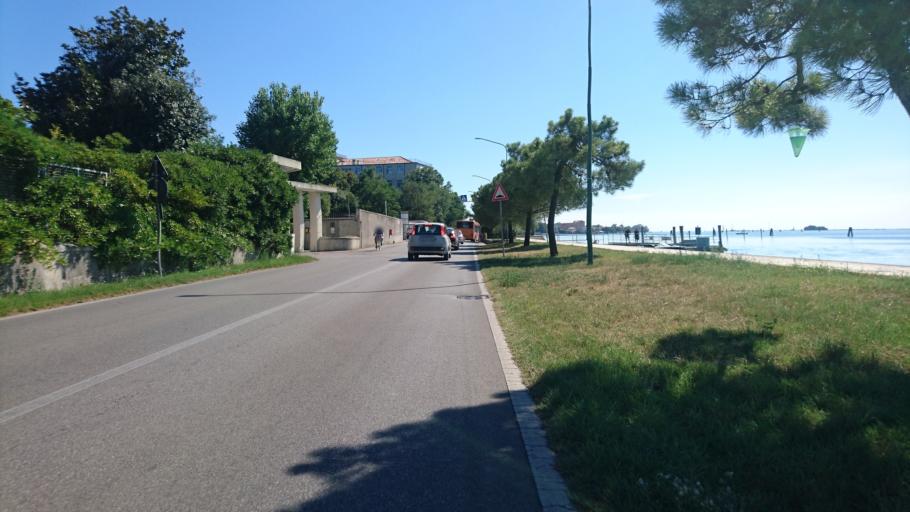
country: IT
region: Veneto
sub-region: Provincia di Venezia
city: San Pietro in Volta
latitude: 45.3559
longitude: 12.3275
